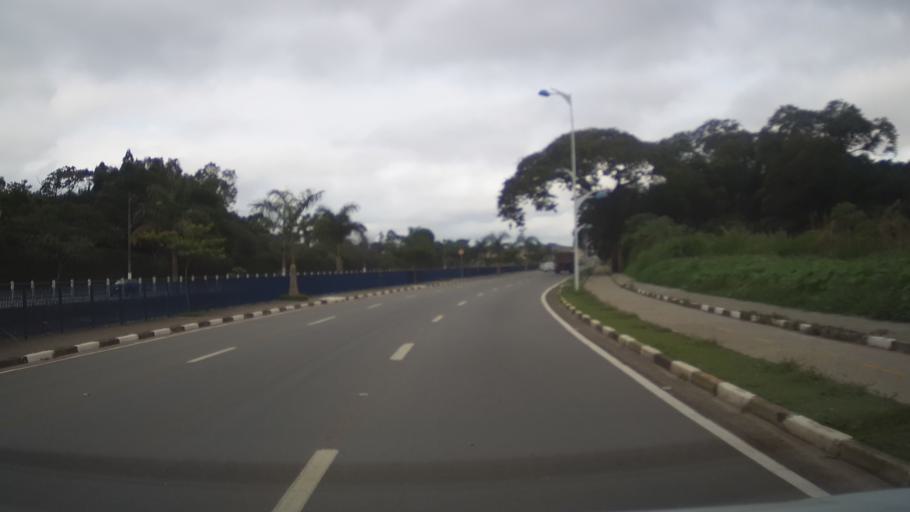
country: BR
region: Sao Paulo
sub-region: Aruja
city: Aruja
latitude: -23.4129
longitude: -46.3694
